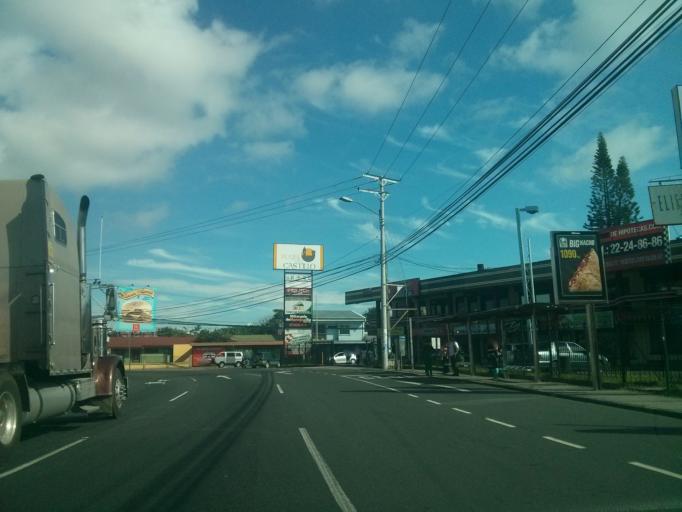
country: CR
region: San Jose
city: San Pedro
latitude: 9.9200
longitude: -84.0516
